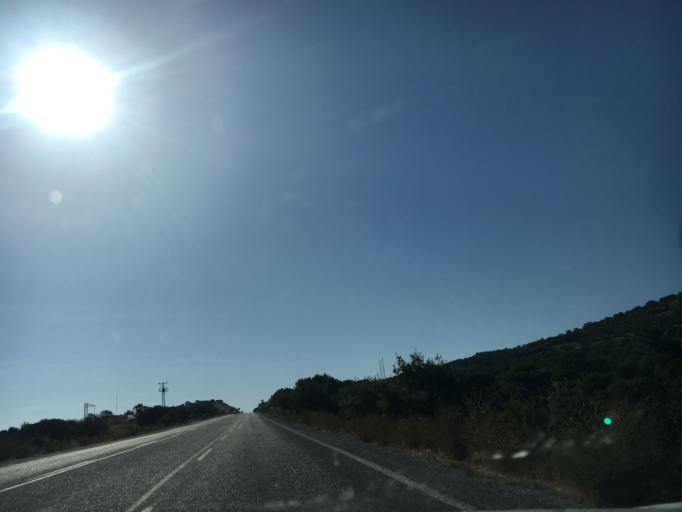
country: TR
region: Canakkale
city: Behram
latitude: 39.5051
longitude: 26.3986
